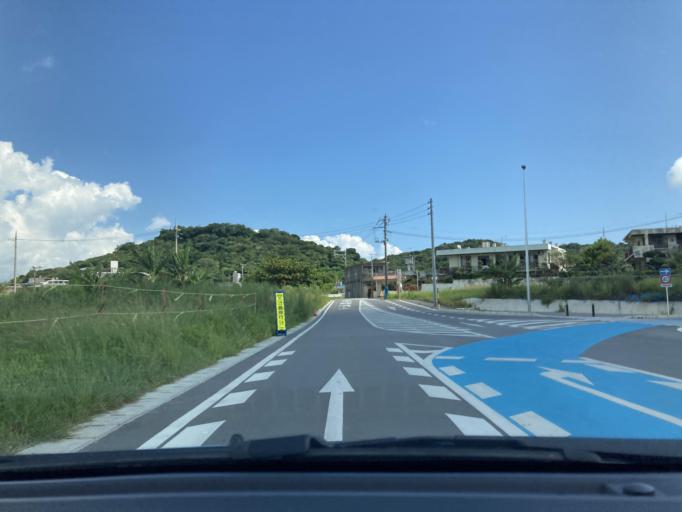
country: JP
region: Okinawa
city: Tomigusuku
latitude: 26.1608
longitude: 127.7561
